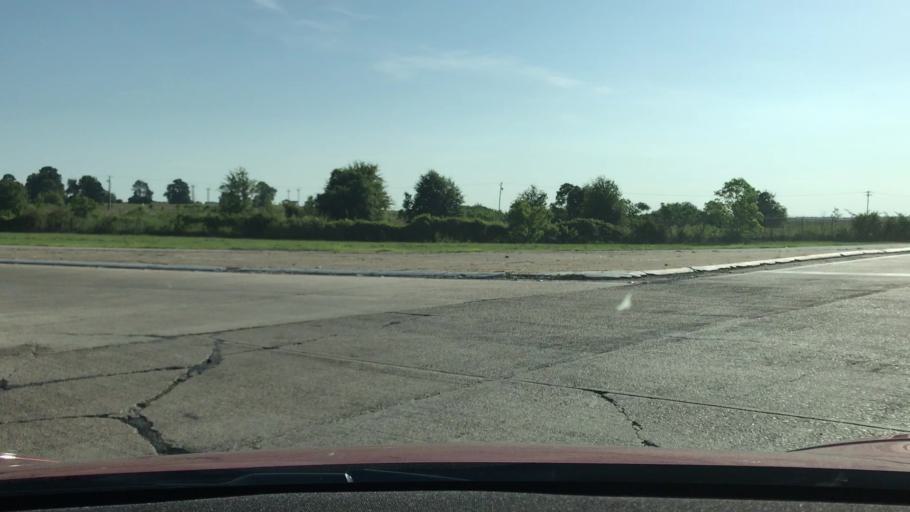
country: US
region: Louisiana
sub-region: Caddo Parish
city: Shreveport
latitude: 32.4422
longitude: -93.8413
